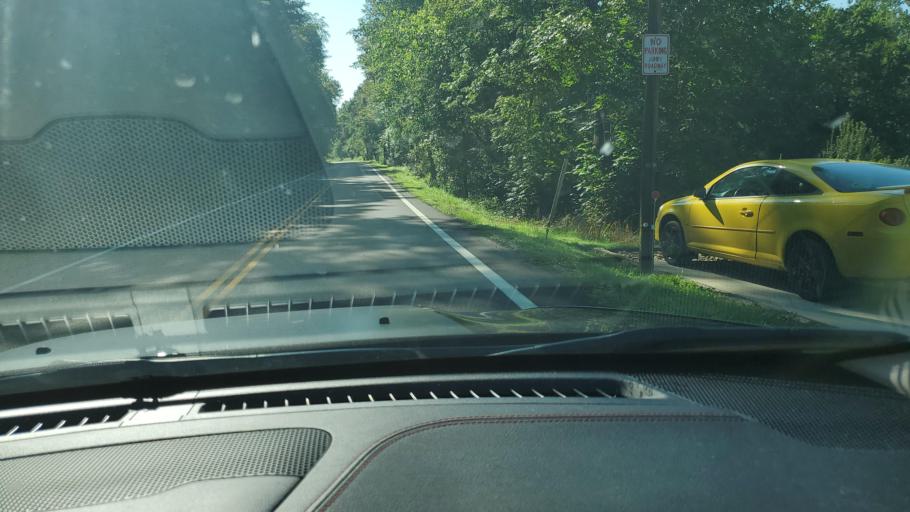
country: US
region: Ohio
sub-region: Mahoning County
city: Lowellville
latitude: 41.0345
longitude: -80.5272
